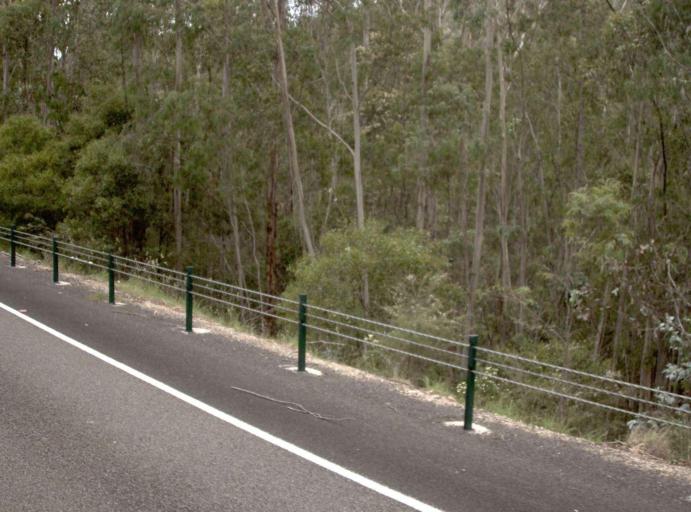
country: AU
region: New South Wales
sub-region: Bombala
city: Bombala
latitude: -37.2886
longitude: 149.2220
